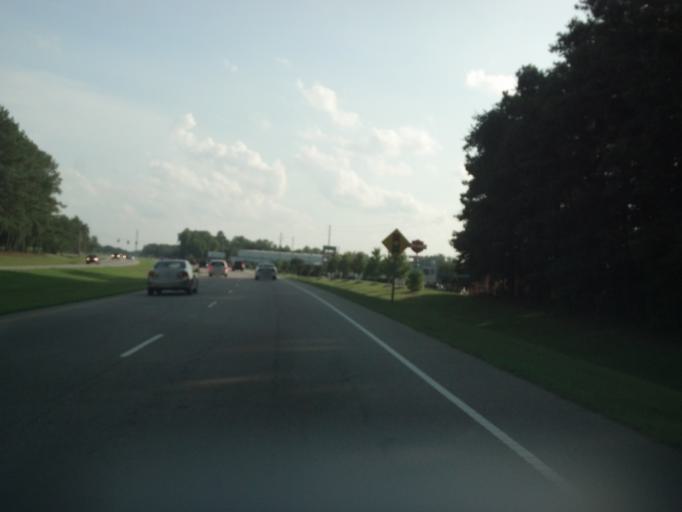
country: US
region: North Carolina
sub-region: Pitt County
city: Winterville
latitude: 35.5381
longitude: -77.4069
